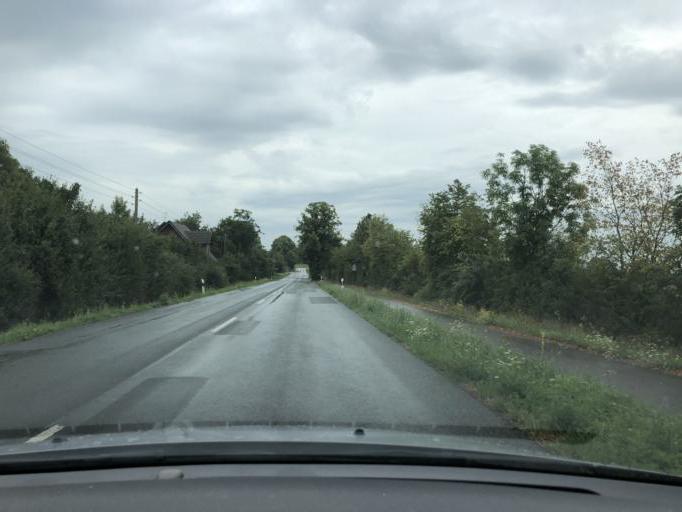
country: DE
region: North Rhine-Westphalia
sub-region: Regierungsbezirk Dusseldorf
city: Schermbeck
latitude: 51.7205
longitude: 6.8697
